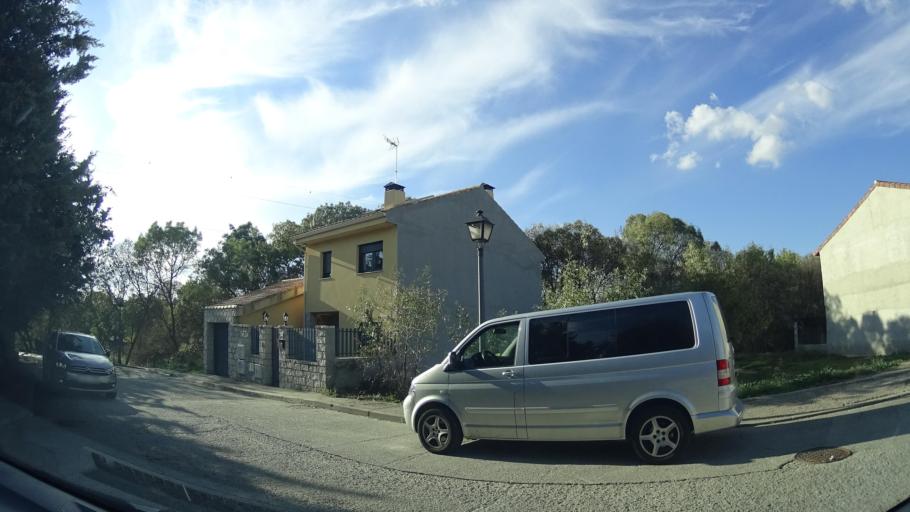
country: ES
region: Madrid
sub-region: Provincia de Madrid
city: Colmenarejo
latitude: 40.5612
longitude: -4.0225
